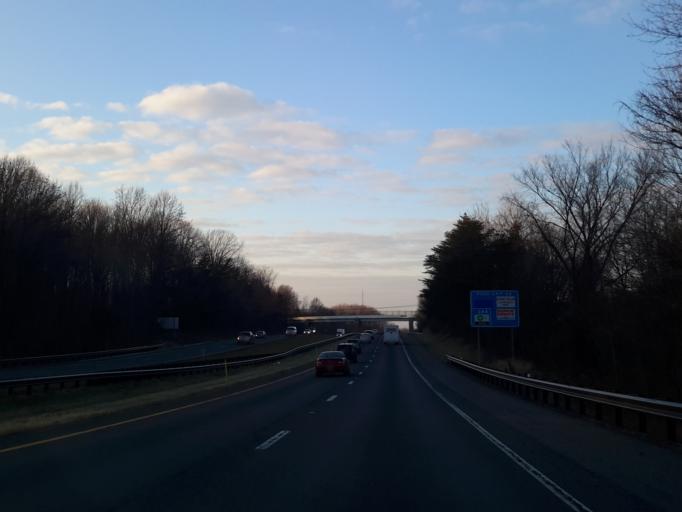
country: US
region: Maryland
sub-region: Montgomery County
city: Clarksburg
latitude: 39.2448
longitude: -77.2963
